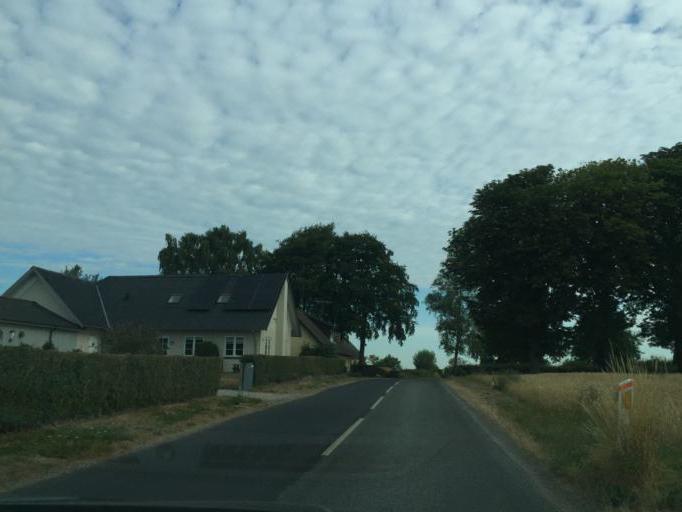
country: DK
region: South Denmark
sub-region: Assens Kommune
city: Assens
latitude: 55.2739
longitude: 9.9769
